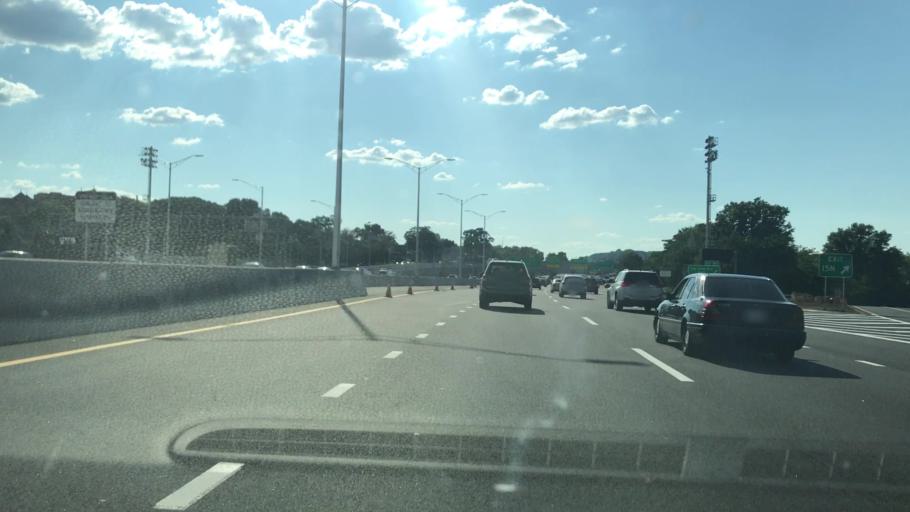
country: US
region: New York
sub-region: Kings County
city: Bensonhurst
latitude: 40.6026
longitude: -74.0635
